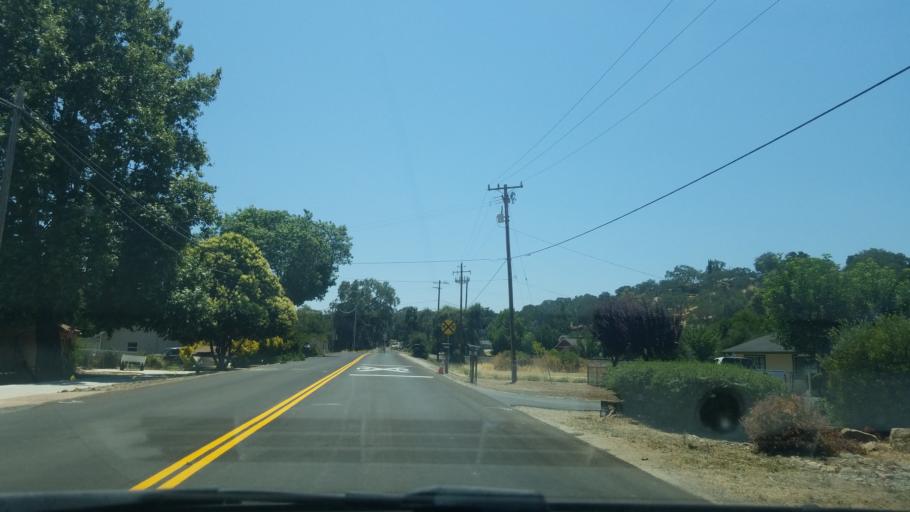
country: US
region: California
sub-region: San Luis Obispo County
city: Atascadero
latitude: 35.4907
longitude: -120.6471
